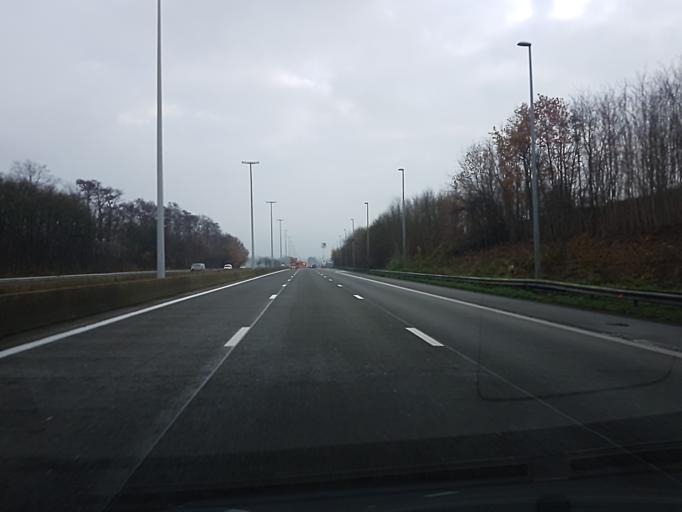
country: BE
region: Flanders
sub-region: Provincie Vlaams-Brabant
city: Tienen
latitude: 50.7572
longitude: 4.9479
